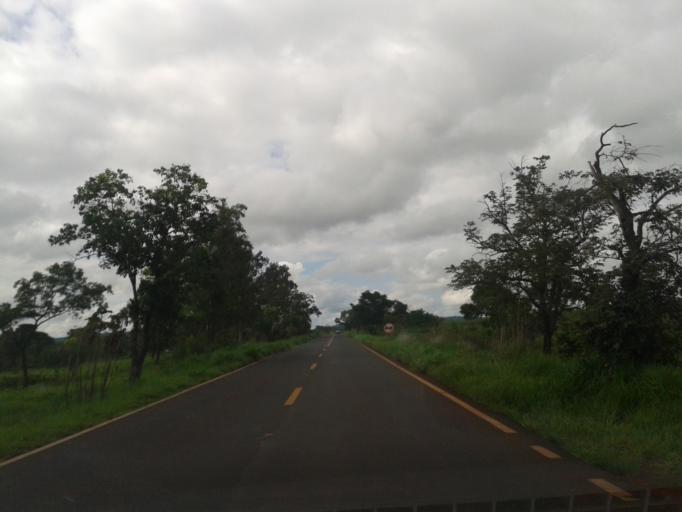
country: BR
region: Minas Gerais
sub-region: Ituiutaba
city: Ituiutaba
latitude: -19.1317
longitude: -49.7740
